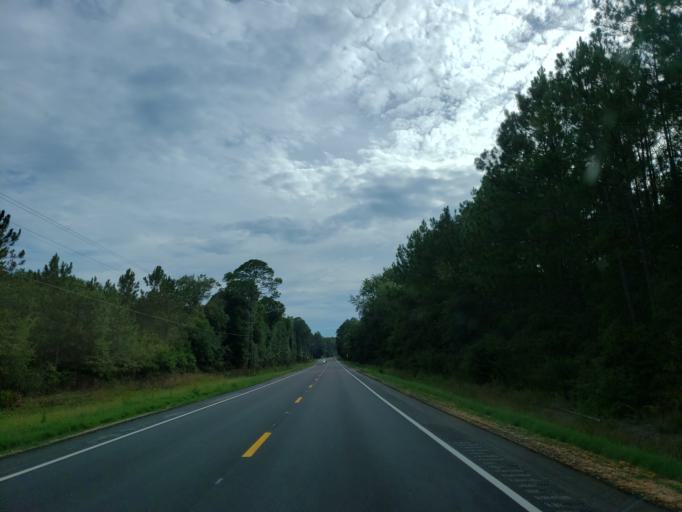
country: US
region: Georgia
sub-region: Irwin County
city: Ocilla
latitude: 31.5710
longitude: -83.3072
